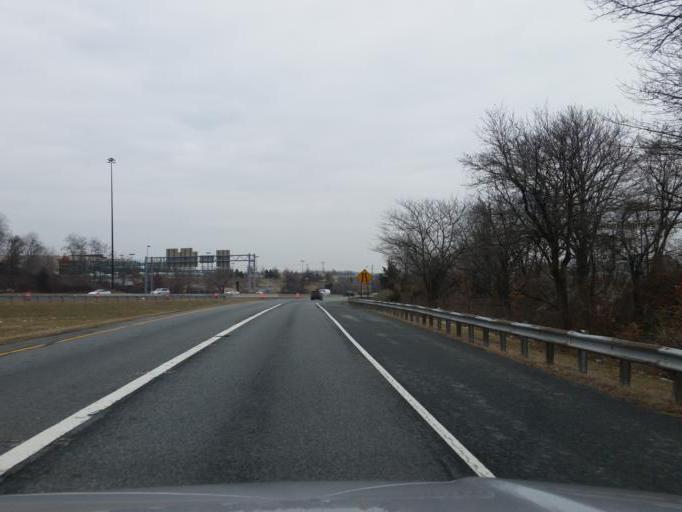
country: US
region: Maryland
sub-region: Baltimore County
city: Lansdowne
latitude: 39.2481
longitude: -76.6784
